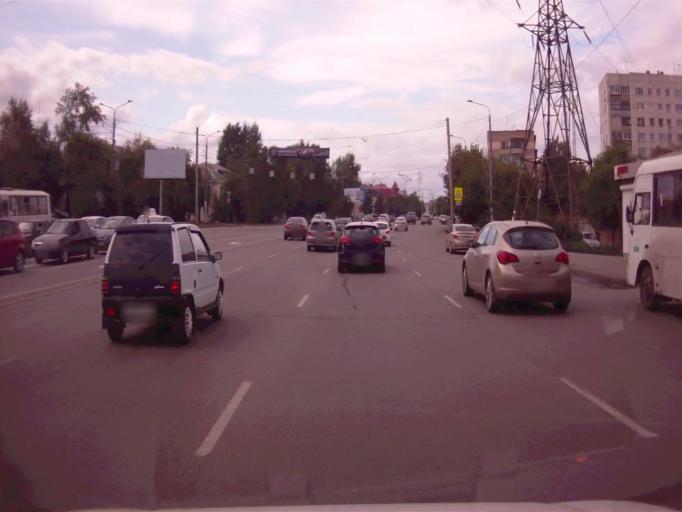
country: RU
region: Chelyabinsk
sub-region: Gorod Chelyabinsk
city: Chelyabinsk
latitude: 55.1382
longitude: 61.4016
